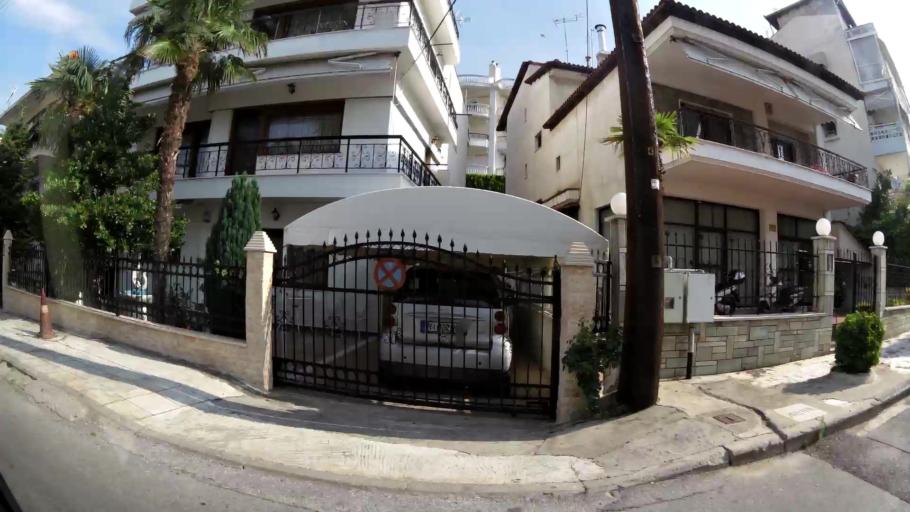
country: GR
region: Central Macedonia
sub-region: Nomos Thessalonikis
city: Agios Pavlos
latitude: 40.6480
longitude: 22.9585
